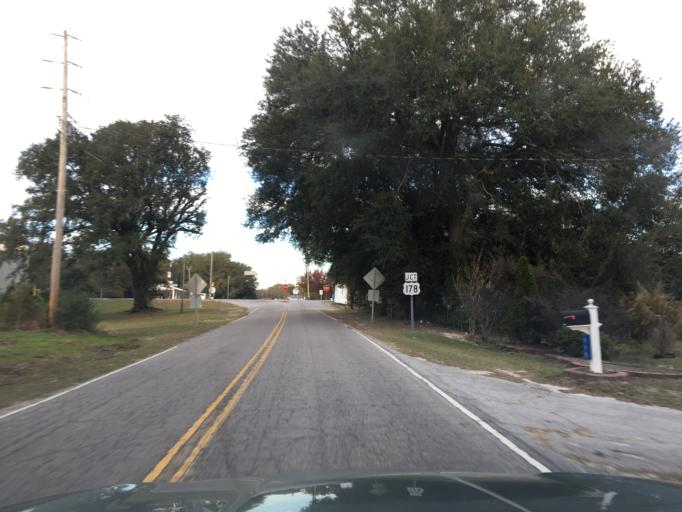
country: US
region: South Carolina
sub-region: Lexington County
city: Leesville
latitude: 33.7579
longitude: -81.3671
